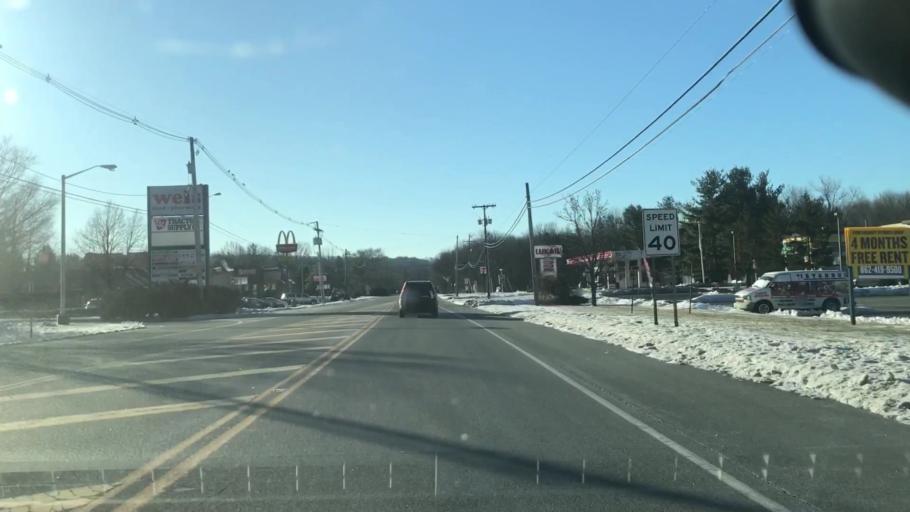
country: US
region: New Jersey
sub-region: Morris County
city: Budd Lake
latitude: 40.8320
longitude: -74.7093
